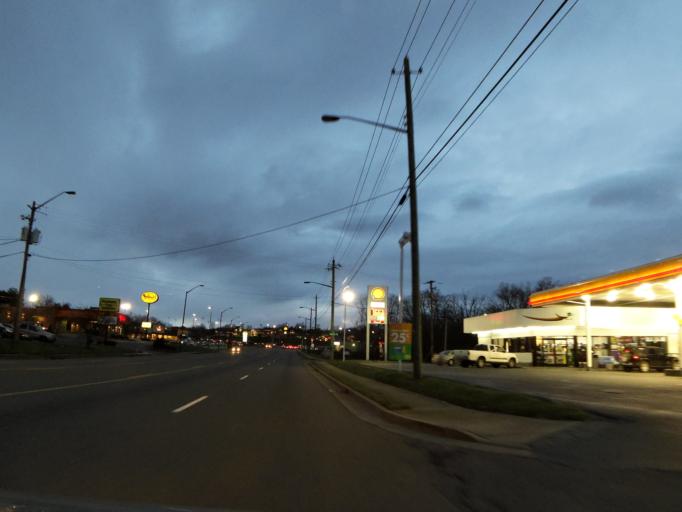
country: US
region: Tennessee
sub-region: Washington County
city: Johnson City
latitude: 36.3027
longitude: -82.3751
